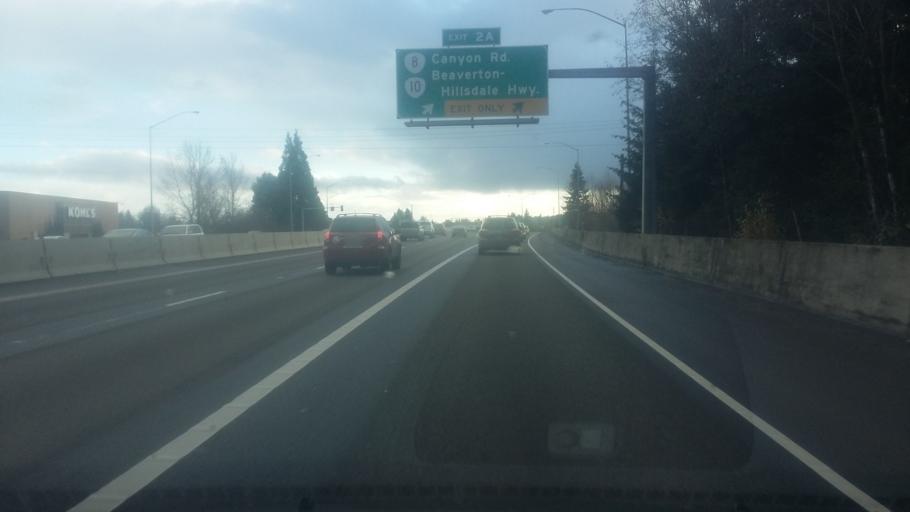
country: US
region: Oregon
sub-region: Washington County
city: Cedar Hills
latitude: 45.4943
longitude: -122.7917
